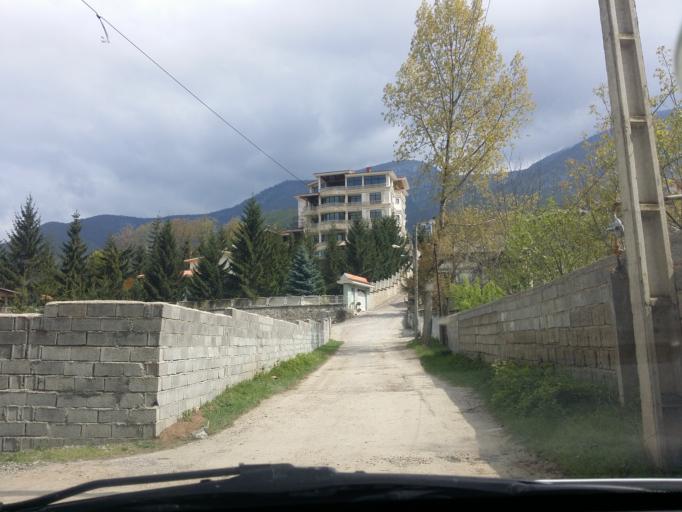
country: IR
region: Mazandaran
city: `Abbasabad
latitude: 36.4961
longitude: 51.1495
